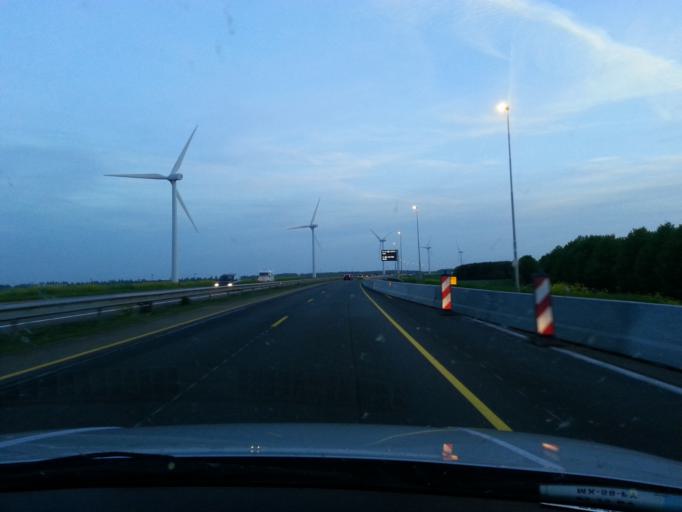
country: NL
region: Utrecht
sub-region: Gemeente Bunschoten
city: Spakenburg
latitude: 52.3279
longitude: 5.3461
